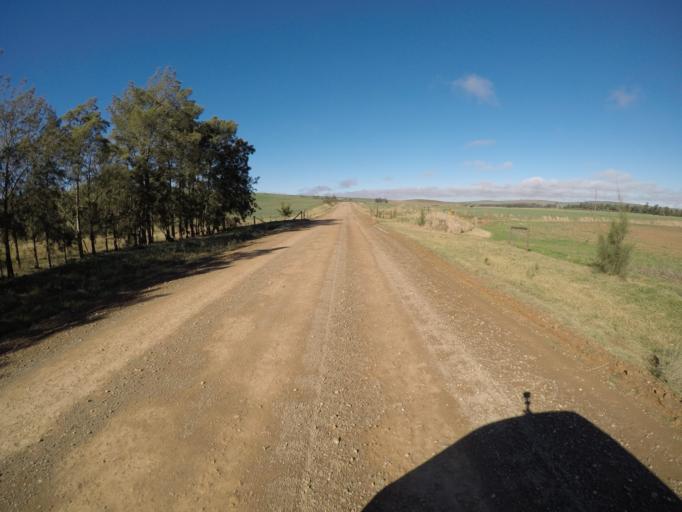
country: ZA
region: Western Cape
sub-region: Overberg District Municipality
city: Caledon
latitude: -34.1008
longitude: 19.7004
